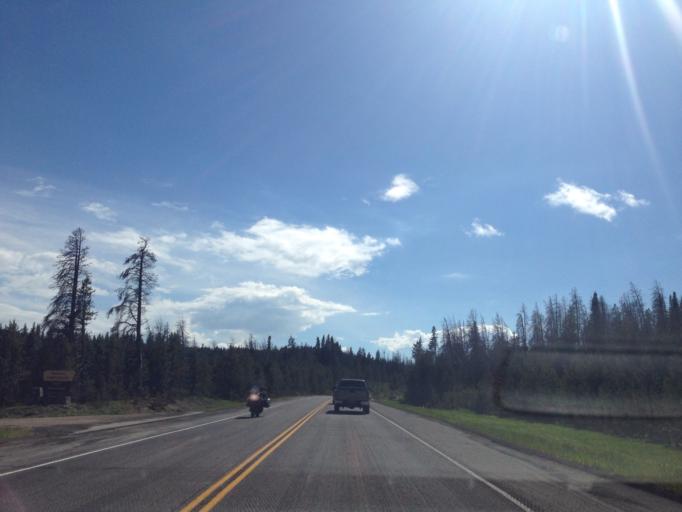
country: US
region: Colorado
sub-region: Routt County
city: Steamboat Springs
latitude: 40.3770
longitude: -106.7218
